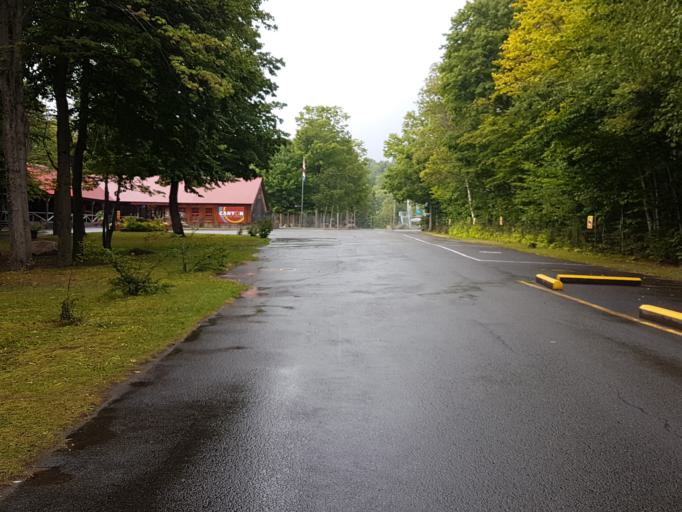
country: CA
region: Quebec
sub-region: Capitale-Nationale
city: Beaupre
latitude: 47.0719
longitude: -70.8740
